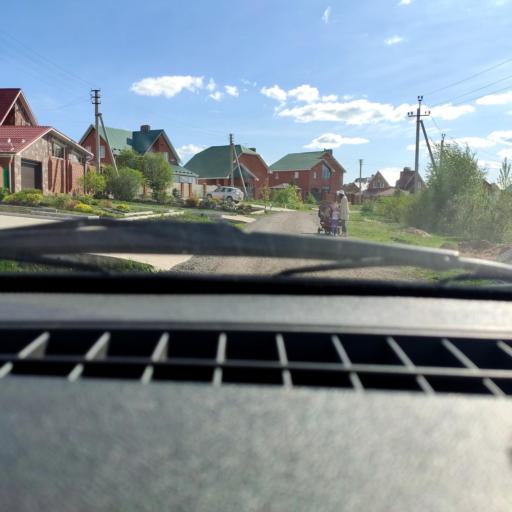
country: RU
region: Bashkortostan
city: Avdon
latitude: 54.6993
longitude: 55.7926
